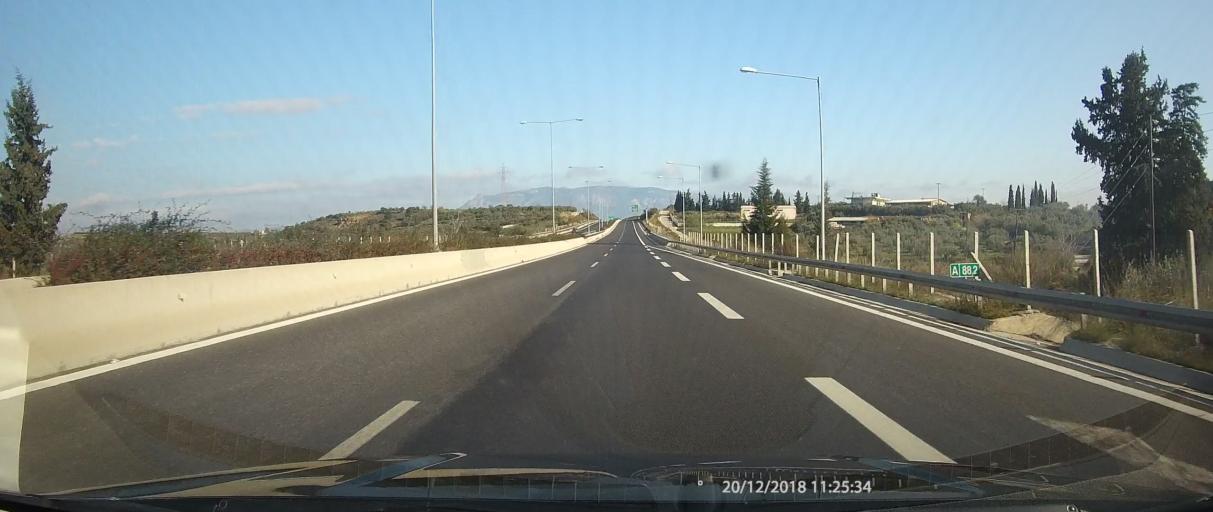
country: GR
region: Peloponnese
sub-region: Nomos Korinthias
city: Arkhaia Korinthos
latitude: 37.9003
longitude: 22.9004
